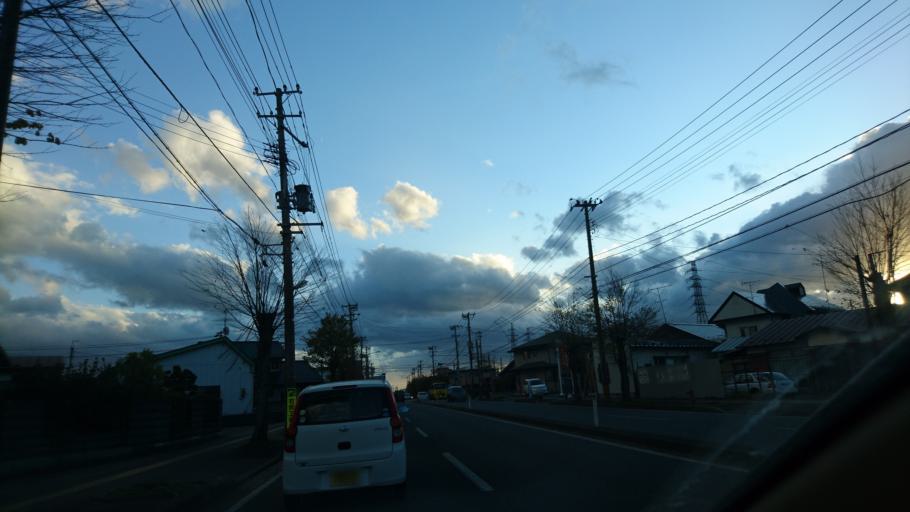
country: JP
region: Iwate
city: Mizusawa
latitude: 39.1446
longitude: 141.1298
